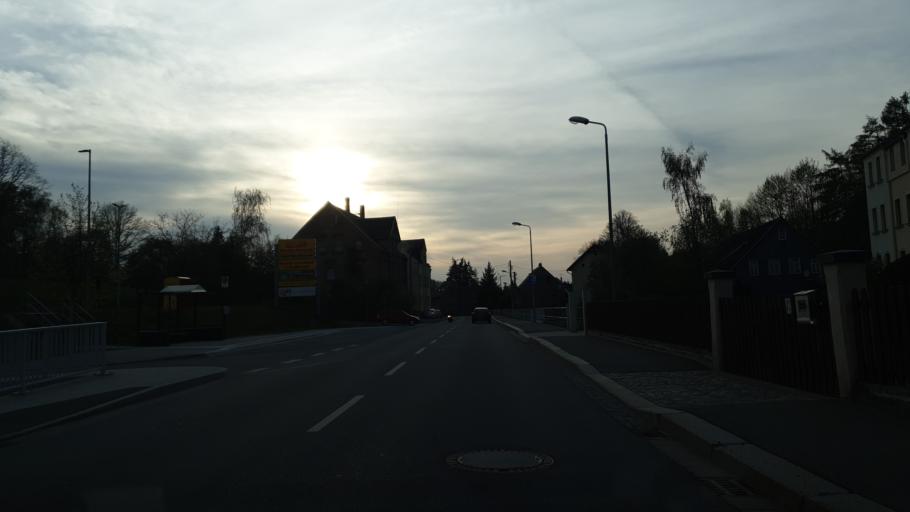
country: DE
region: Saxony
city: Gersdorf
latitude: 50.7490
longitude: 12.7175
